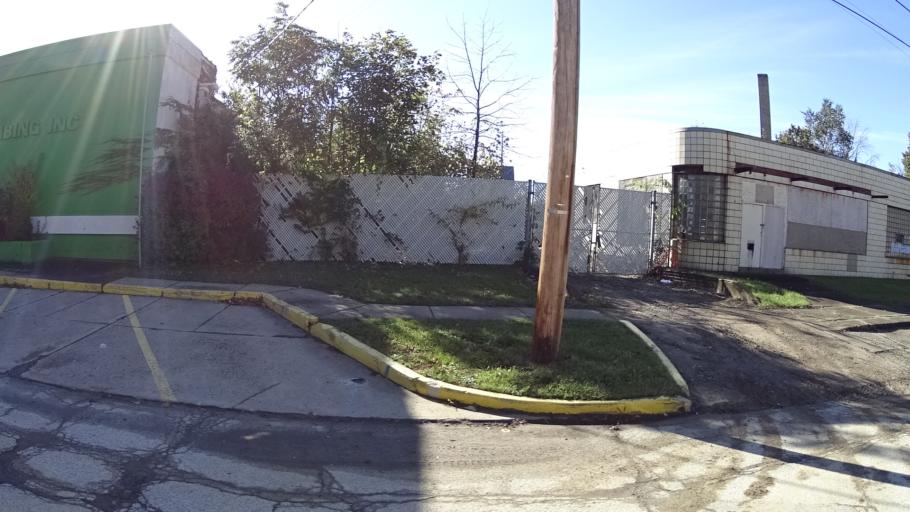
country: US
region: Ohio
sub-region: Lorain County
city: Lorain
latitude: 41.4397
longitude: -82.1620
